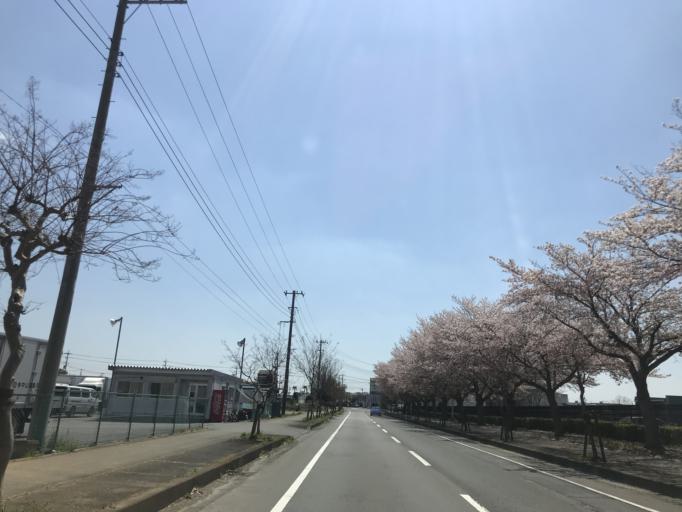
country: JP
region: Ibaraki
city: Moriya
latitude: 35.9499
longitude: 139.9682
